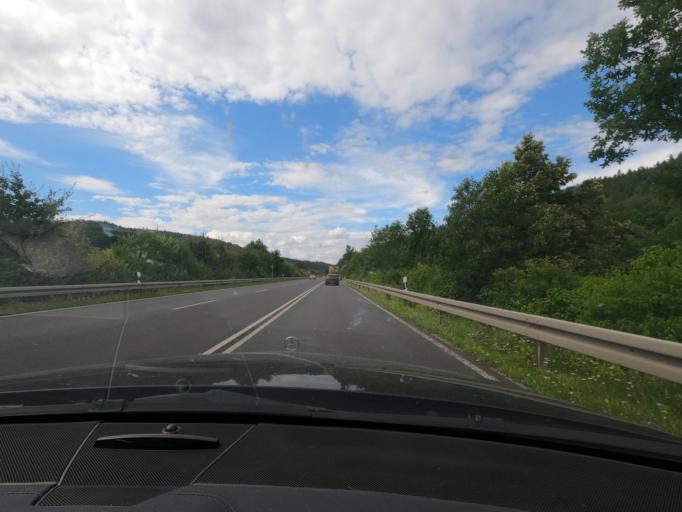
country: DE
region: Hesse
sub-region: Regierungsbezirk Kassel
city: Burghaun
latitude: 50.7295
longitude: 9.7008
